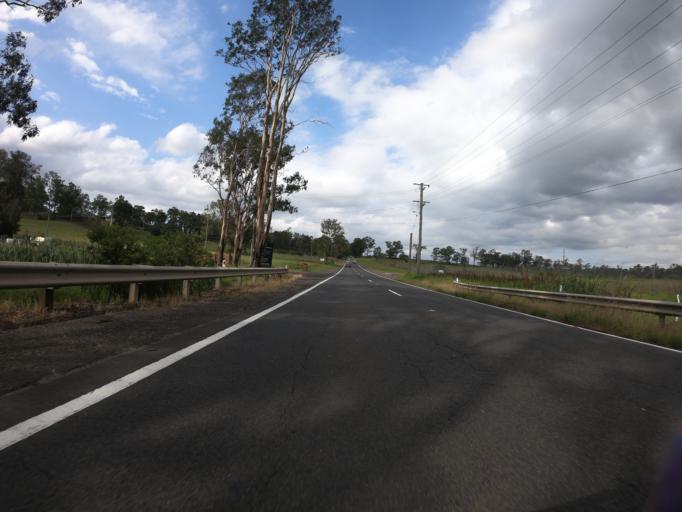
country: AU
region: New South Wales
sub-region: Blacktown
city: Riverstone
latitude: -33.6671
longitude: 150.8847
